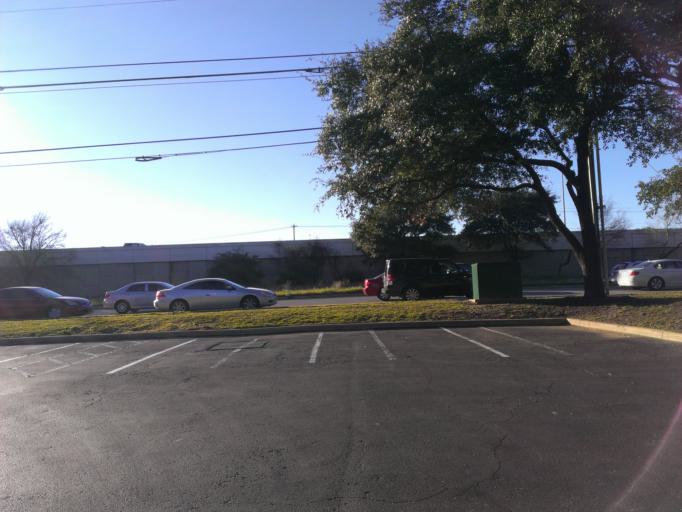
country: US
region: Texas
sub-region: Williamson County
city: Jollyville
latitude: 30.3957
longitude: -97.7456
